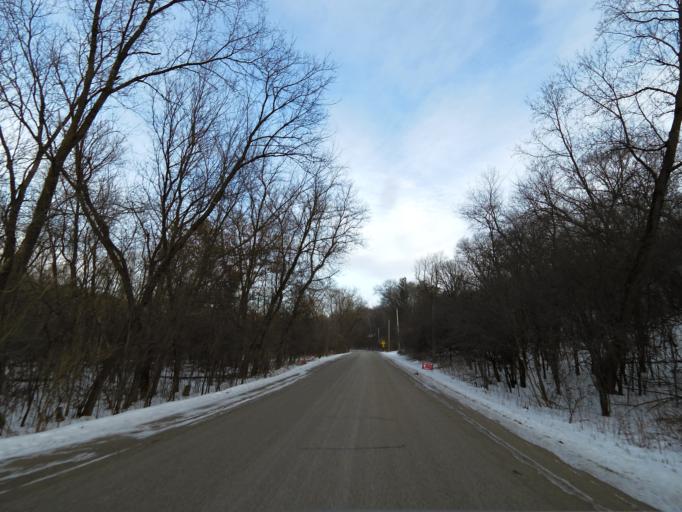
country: US
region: Minnesota
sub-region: Washington County
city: Afton
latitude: 44.9147
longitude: -92.8143
